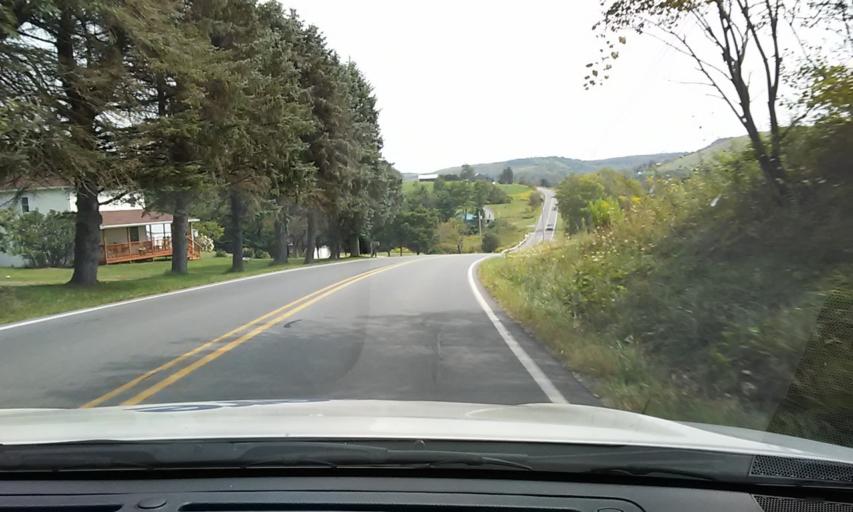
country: US
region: Pennsylvania
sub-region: Elk County
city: Ridgway
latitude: 41.3125
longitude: -78.6578
